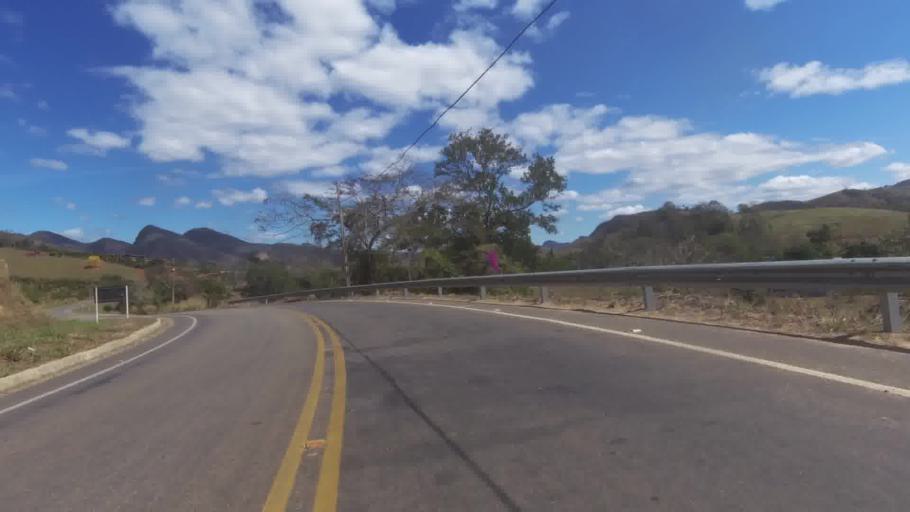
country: BR
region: Espirito Santo
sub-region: Cachoeiro De Itapemirim
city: Cachoeiro de Itapemirim
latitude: -20.9121
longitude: -41.2091
